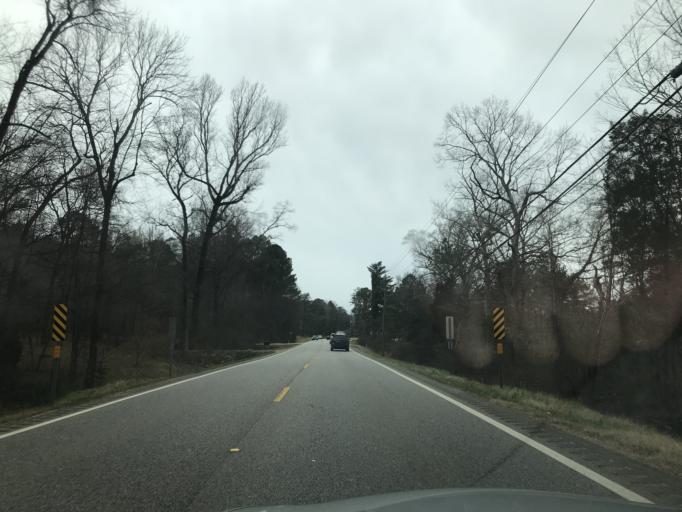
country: US
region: Alabama
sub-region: Shelby County
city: Meadowbrook
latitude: 33.3828
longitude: -86.6997
